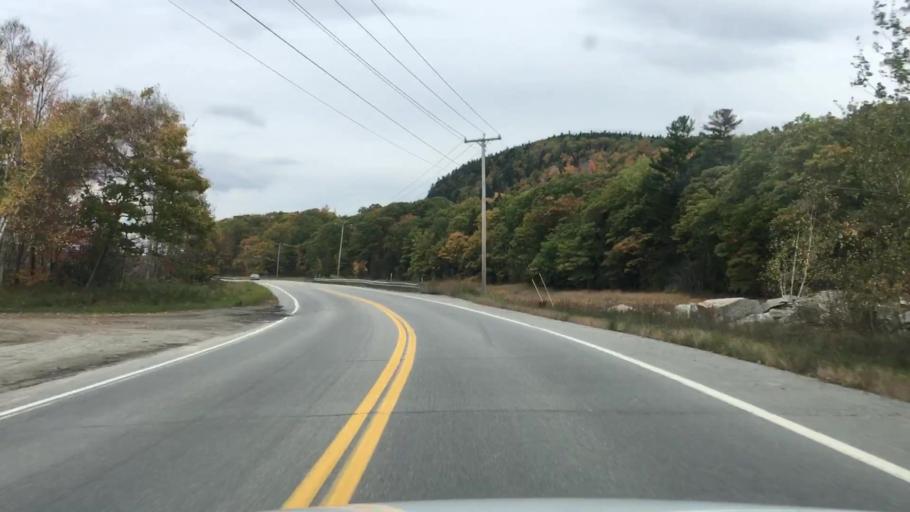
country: US
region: Maine
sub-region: Waldo County
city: Frankfort
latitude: 44.5905
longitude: -68.8658
